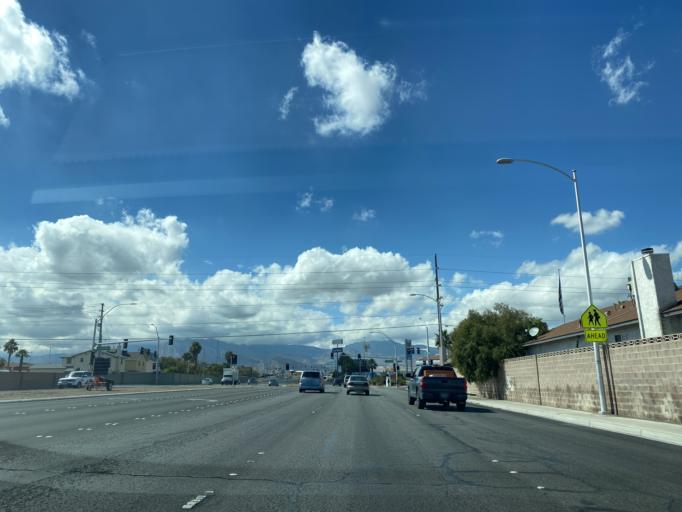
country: US
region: Nevada
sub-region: Clark County
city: Las Vegas
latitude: 36.2405
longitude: -115.2410
